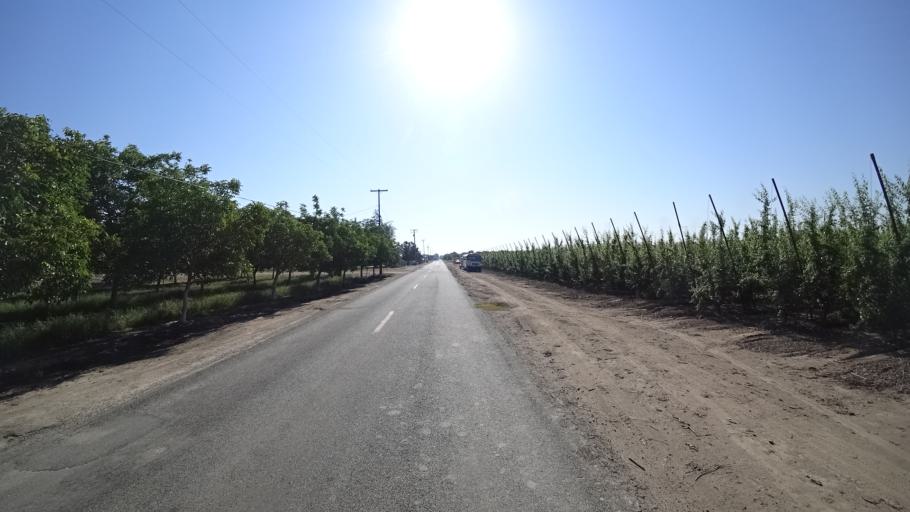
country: US
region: California
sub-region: Kings County
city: Lucerne
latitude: 36.3863
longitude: -119.6670
